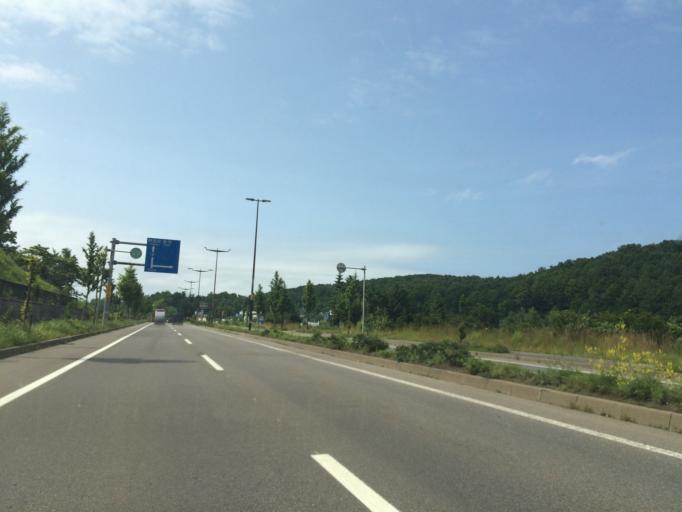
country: JP
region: Hokkaido
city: Otaru
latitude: 43.2156
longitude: 140.9567
